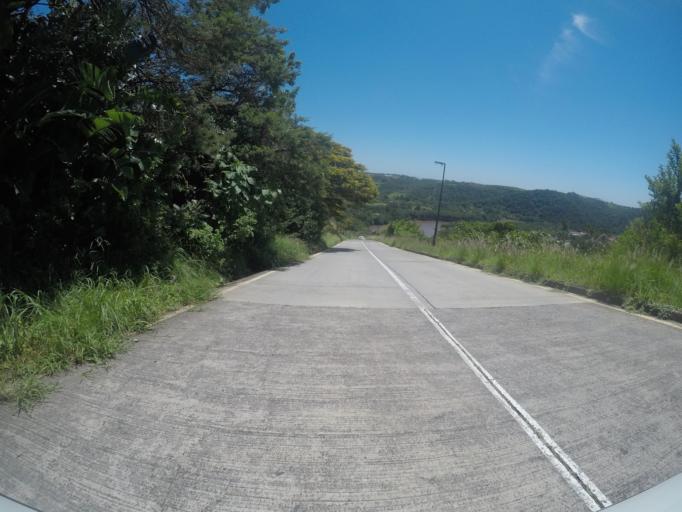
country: ZA
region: Eastern Cape
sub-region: Buffalo City Metropolitan Municipality
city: East London
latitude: -32.9315
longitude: 27.9943
